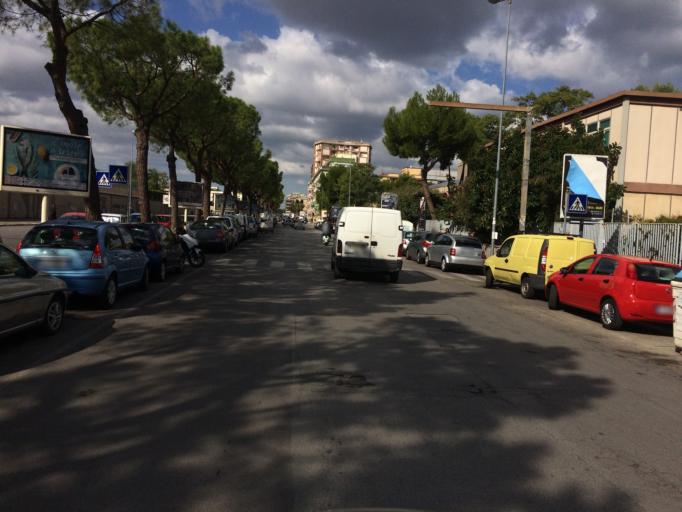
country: IT
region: Apulia
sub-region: Provincia di Bari
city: Bari
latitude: 41.1072
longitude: 16.8700
